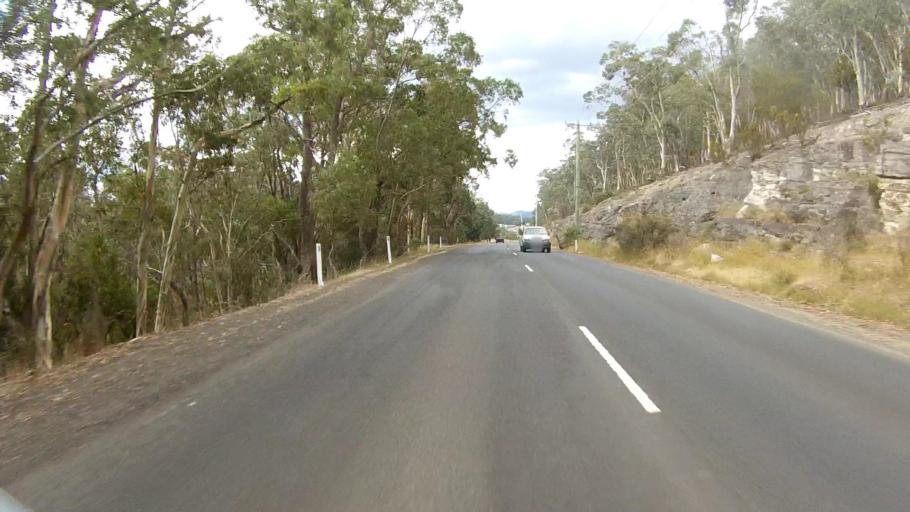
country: AU
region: Tasmania
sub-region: Hobart
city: Dynnyrne
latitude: -42.9034
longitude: 147.2899
